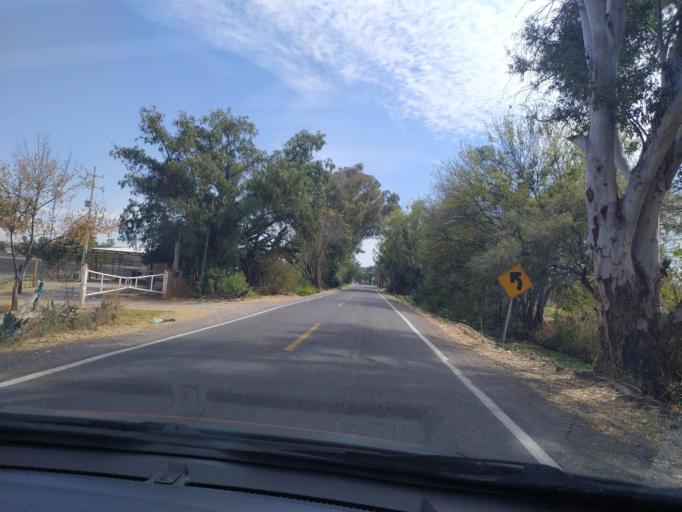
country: MX
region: Guanajuato
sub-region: San Francisco del Rincon
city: San Ignacio de Hidalgo
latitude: 20.8818
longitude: -101.8631
